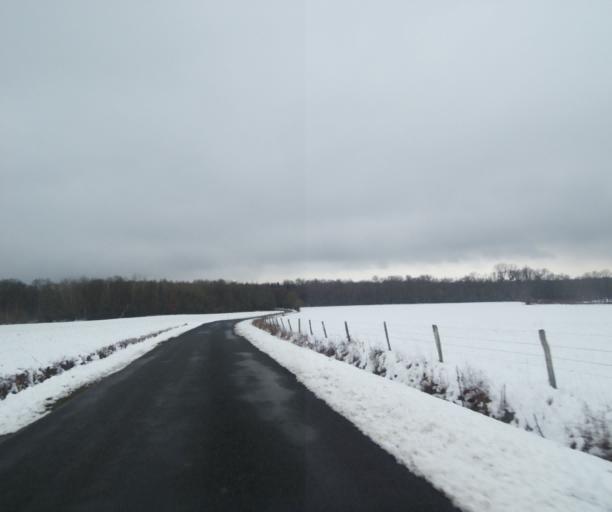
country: FR
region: Champagne-Ardenne
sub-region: Departement de la Haute-Marne
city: Laneuville-a-Remy
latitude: 48.4904
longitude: 4.8674
